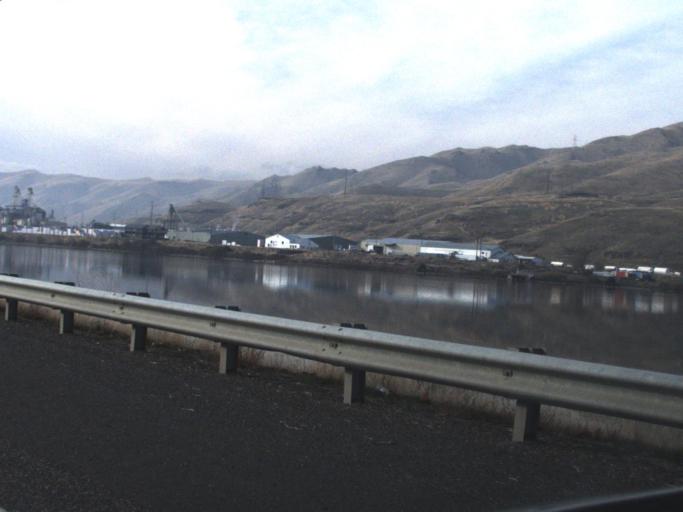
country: US
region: Washington
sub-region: Asotin County
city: West Clarkston-Highland
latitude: 46.4198
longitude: -117.0769
